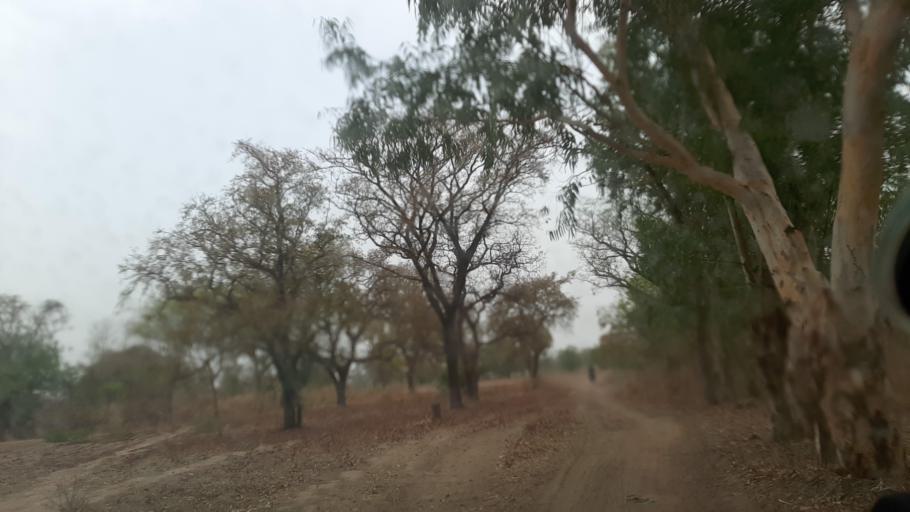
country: BF
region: Boucle du Mouhoun
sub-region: Province des Banwa
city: Salanso
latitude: 11.8502
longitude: -4.4250
